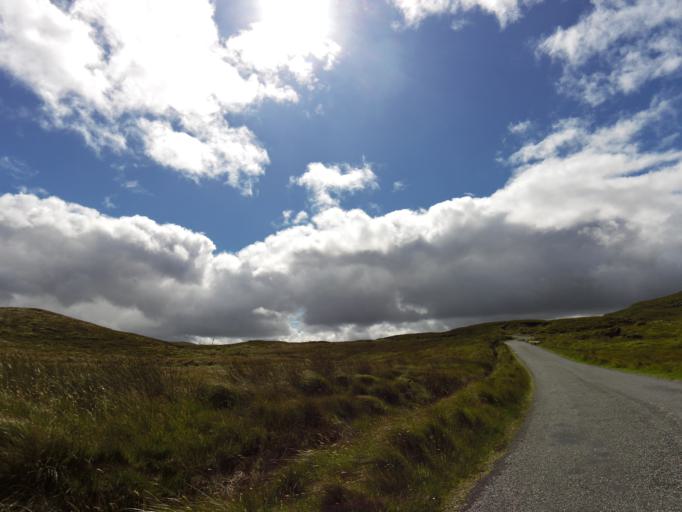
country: IE
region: Connaught
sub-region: County Galway
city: Oughterard
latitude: 53.3963
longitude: -9.3347
